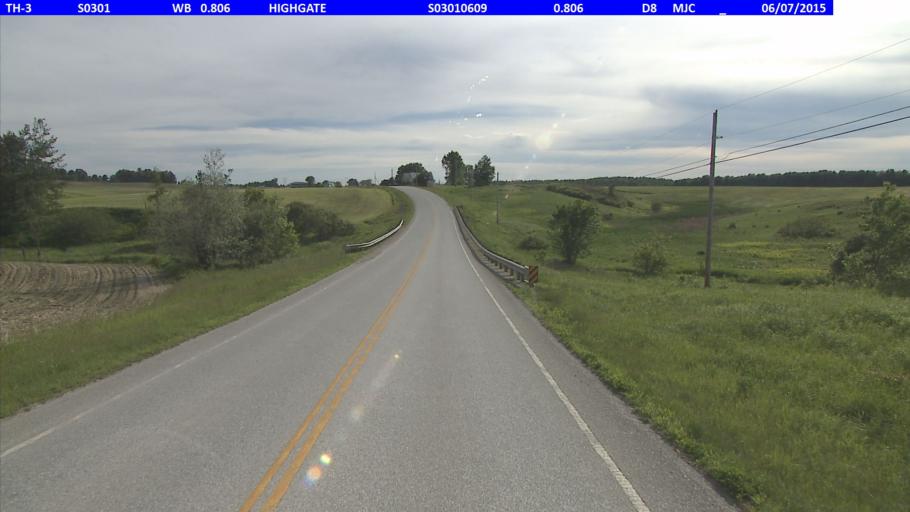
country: US
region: Vermont
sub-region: Franklin County
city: Swanton
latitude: 44.9542
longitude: -73.0029
